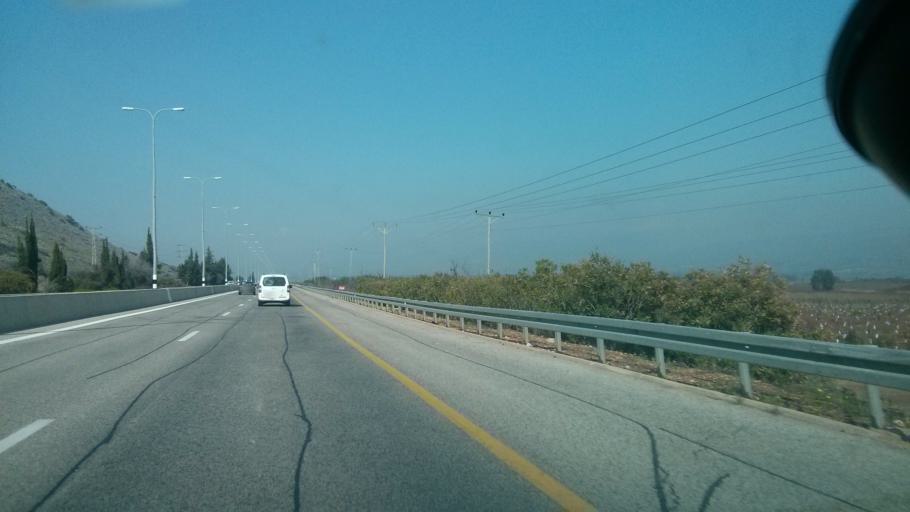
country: IL
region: Northern District
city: Rosh Pinna
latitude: 33.0615
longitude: 35.5746
